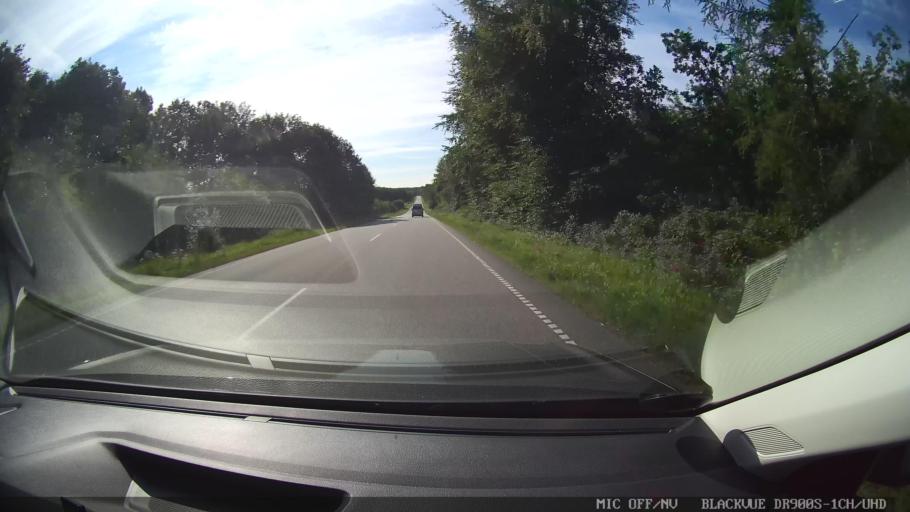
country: DK
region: North Denmark
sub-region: Mariagerfjord Kommune
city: Hadsund
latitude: 56.7453
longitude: 10.0750
